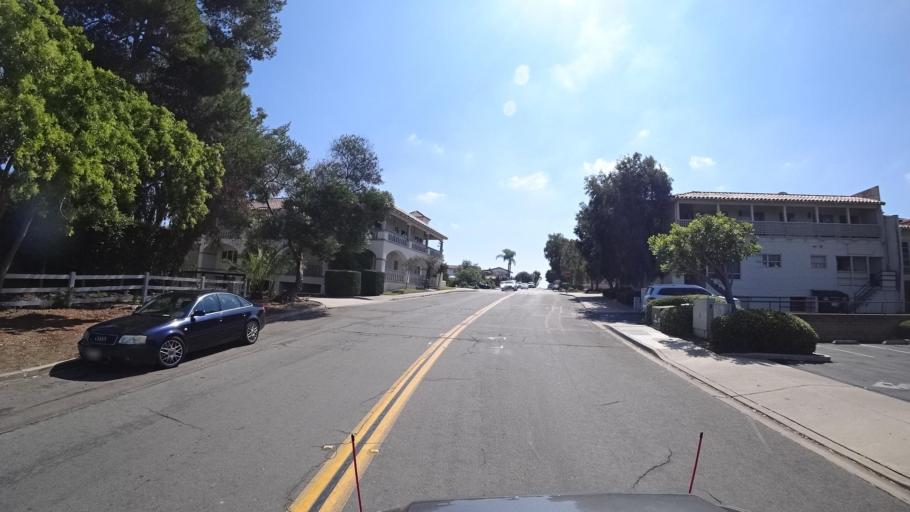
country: US
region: California
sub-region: San Diego County
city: Rancho Santa Fe
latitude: 33.0212
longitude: -117.2041
